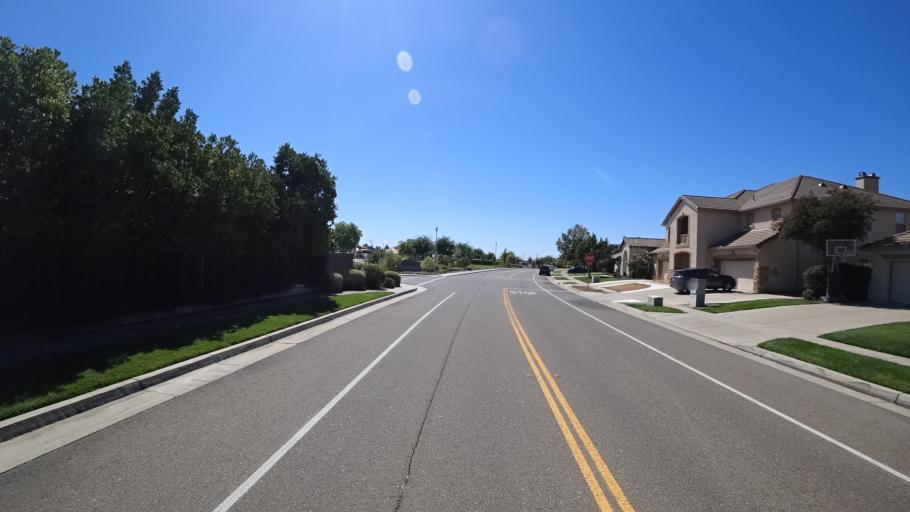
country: US
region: California
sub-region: Sacramento County
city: Elk Grove
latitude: 38.4039
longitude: -121.3390
